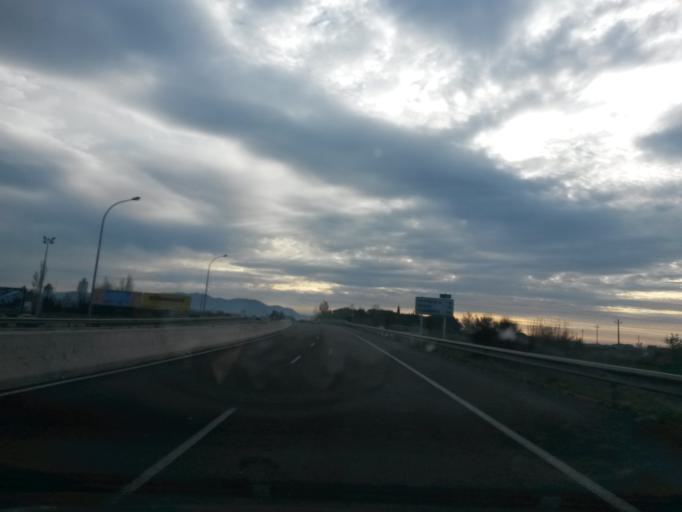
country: ES
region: Catalonia
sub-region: Provincia de Girona
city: Vila-sacra
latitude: 42.2676
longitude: 3.0020
